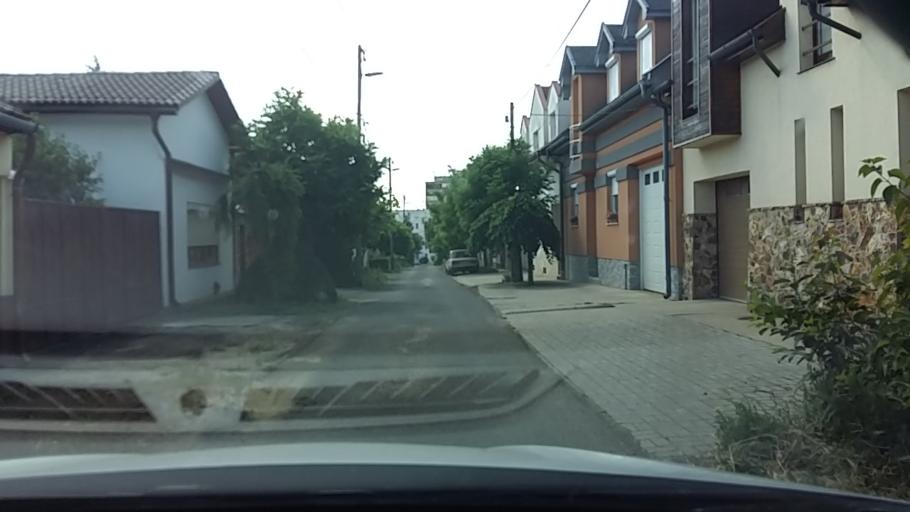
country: HU
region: Heves
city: Gyongyos
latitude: 47.7787
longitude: 19.9322
